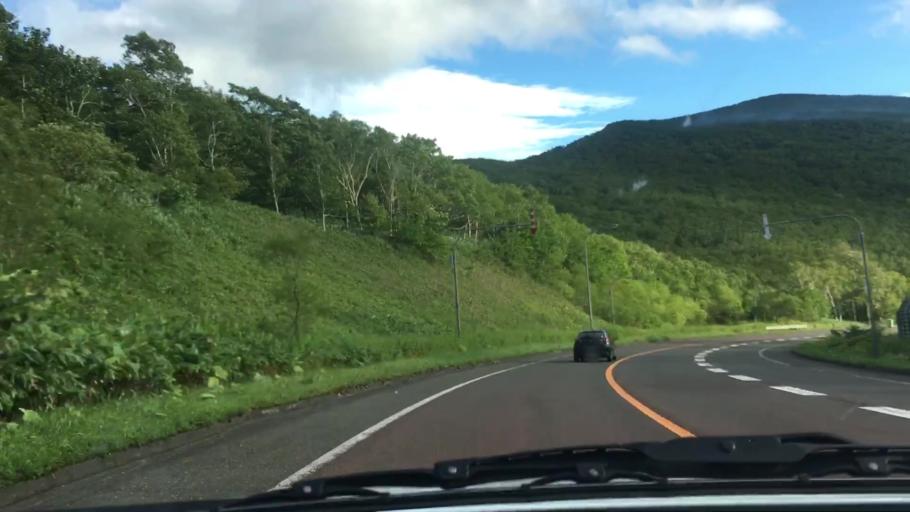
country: JP
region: Hokkaido
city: Shimo-furano
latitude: 43.1303
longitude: 142.7632
